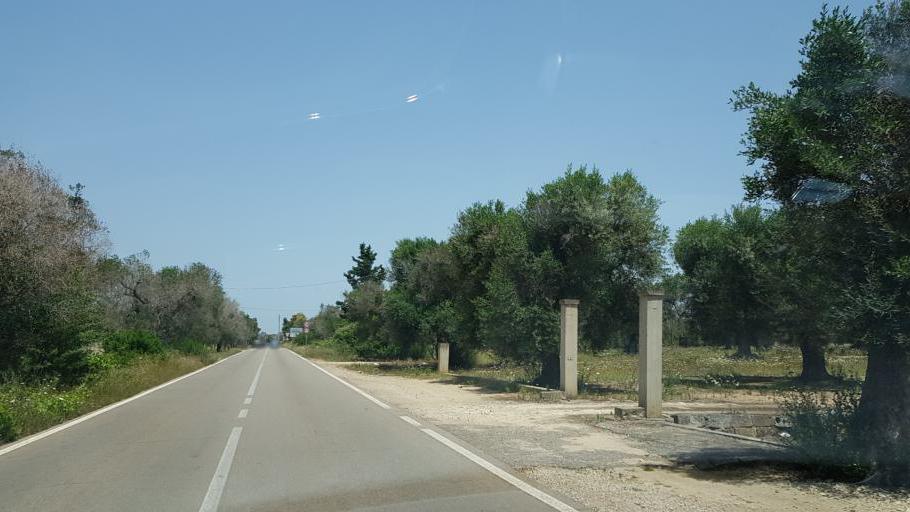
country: IT
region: Apulia
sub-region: Provincia di Lecce
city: Veglie
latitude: 40.3234
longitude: 17.9247
